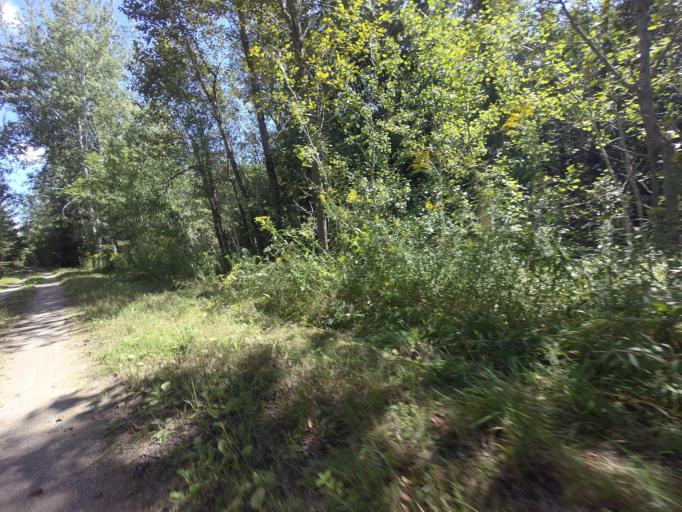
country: CA
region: Ontario
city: Orangeville
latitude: 43.7738
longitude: -80.1845
